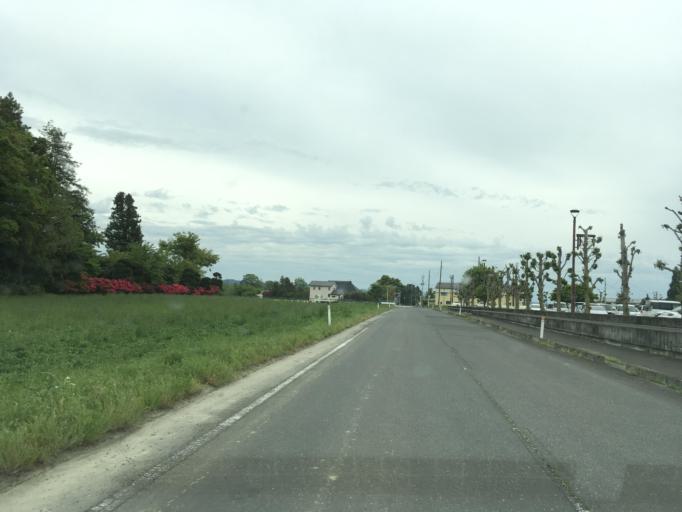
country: JP
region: Miyagi
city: Wakuya
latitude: 38.7155
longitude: 141.2397
